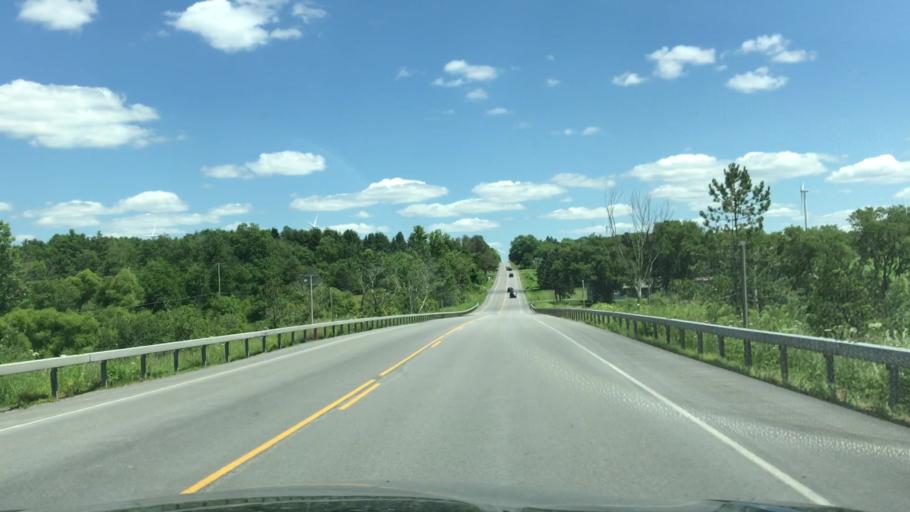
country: US
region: New York
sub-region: Erie County
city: Alden
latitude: 42.7697
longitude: -78.4417
